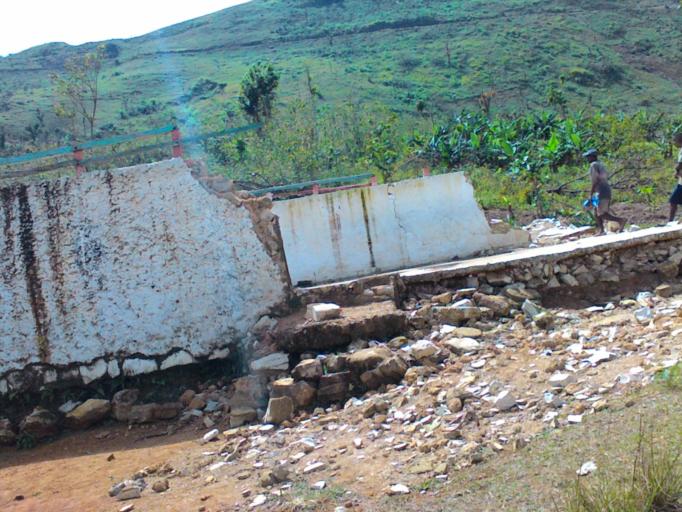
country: HT
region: Grandans
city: Moron
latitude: 18.4530
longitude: -74.1052
